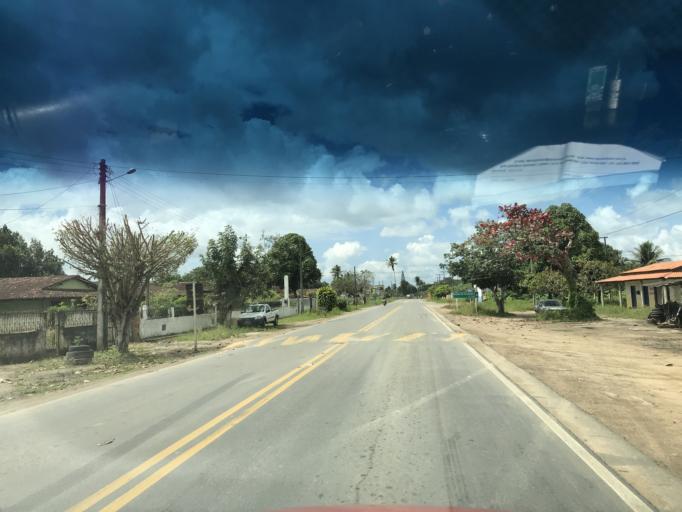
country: BR
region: Bahia
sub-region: Conceicao Do Almeida
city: Conceicao do Almeida
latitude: -12.7295
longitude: -39.1970
